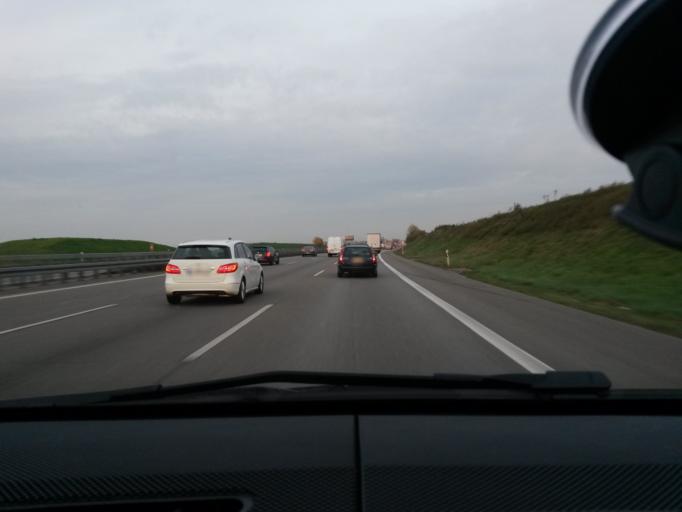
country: DE
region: Baden-Wuerttemberg
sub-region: Regierungsbezirk Stuttgart
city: Neuhausen auf den Fildern
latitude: 48.6958
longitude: 9.2639
